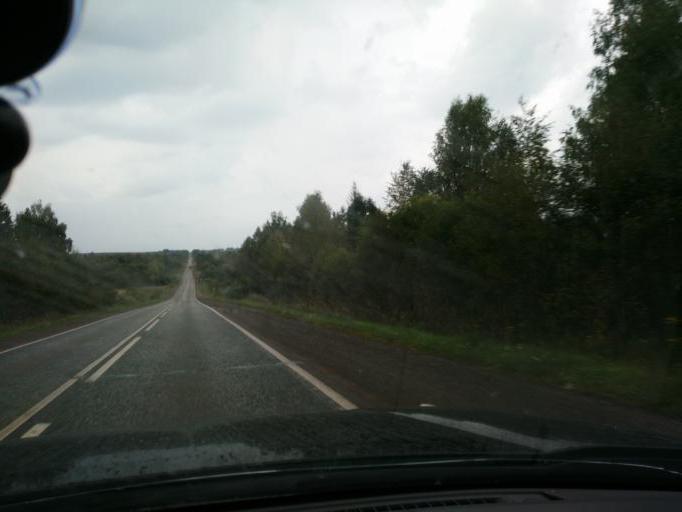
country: RU
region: Perm
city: Barda
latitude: 56.8512
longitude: 55.9452
